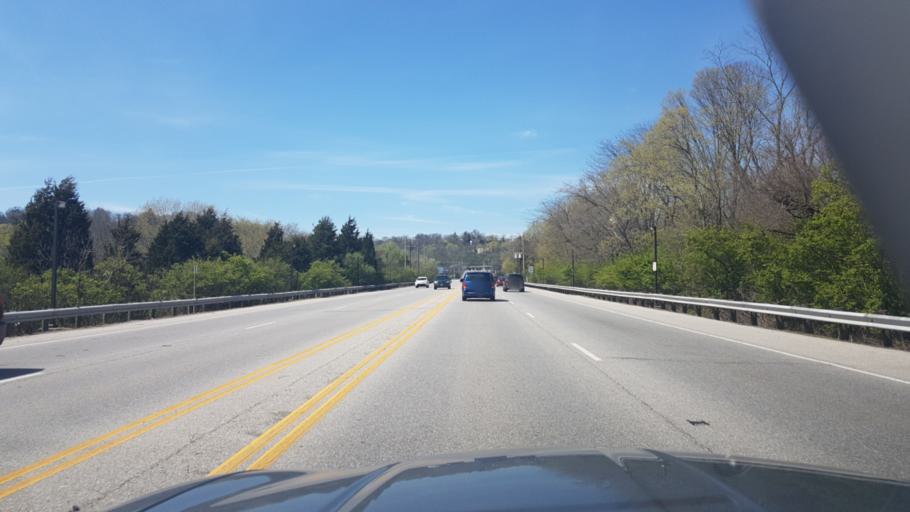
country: US
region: Ohio
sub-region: Hamilton County
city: Turpin Hills
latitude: 39.1163
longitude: -84.4094
